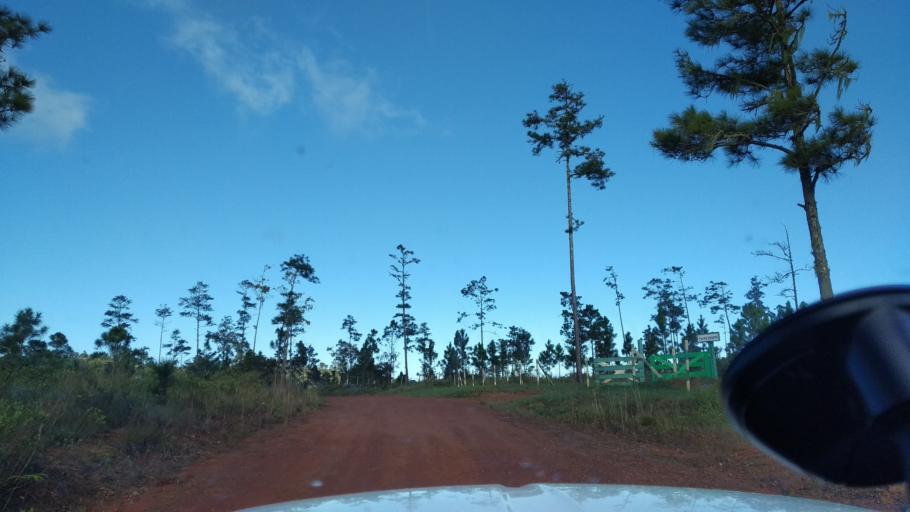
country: BZ
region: Cayo
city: Belmopan
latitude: 16.9982
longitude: -88.8393
